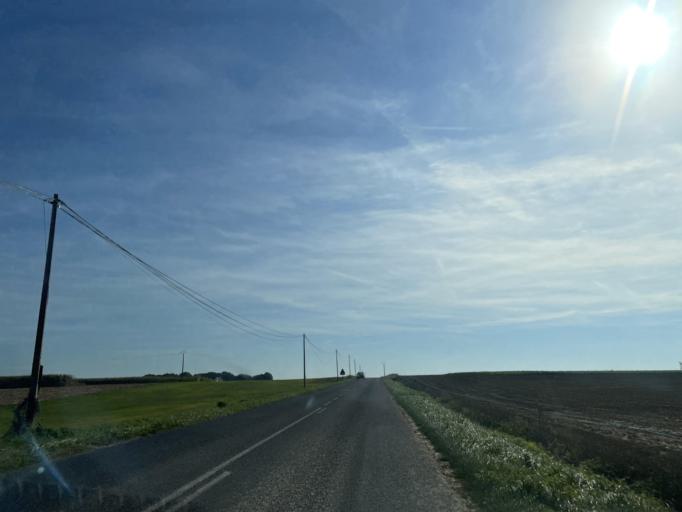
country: FR
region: Ile-de-France
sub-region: Departement de Seine-et-Marne
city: Saint-Jean-les-Deux-Jumeaux
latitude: 48.9068
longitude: 3.0251
